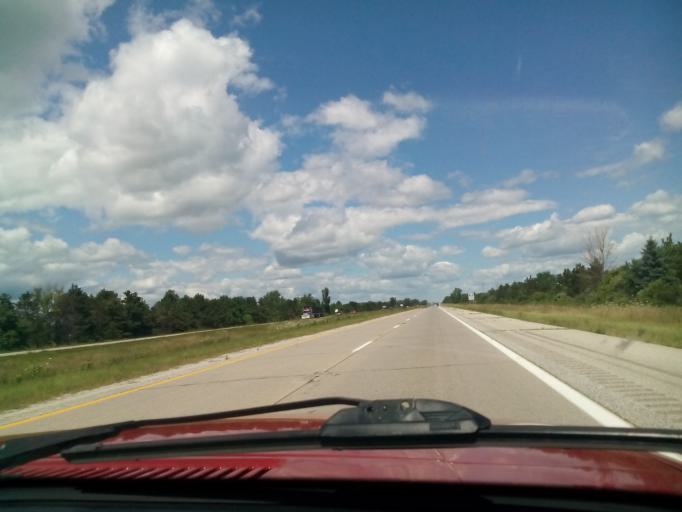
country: US
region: Michigan
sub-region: Bay County
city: Auburn
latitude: 43.6791
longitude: -84.0128
